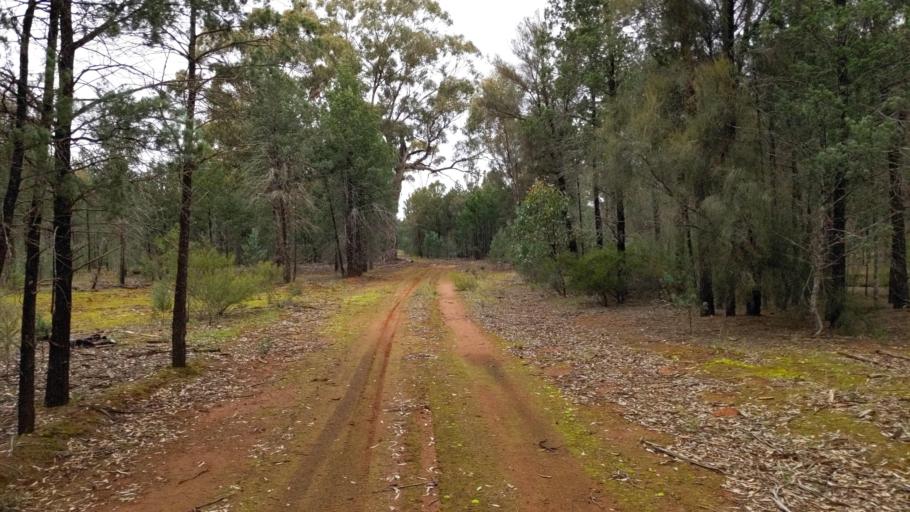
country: AU
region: New South Wales
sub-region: Coolamon
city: Coolamon
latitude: -34.8492
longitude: 146.9321
